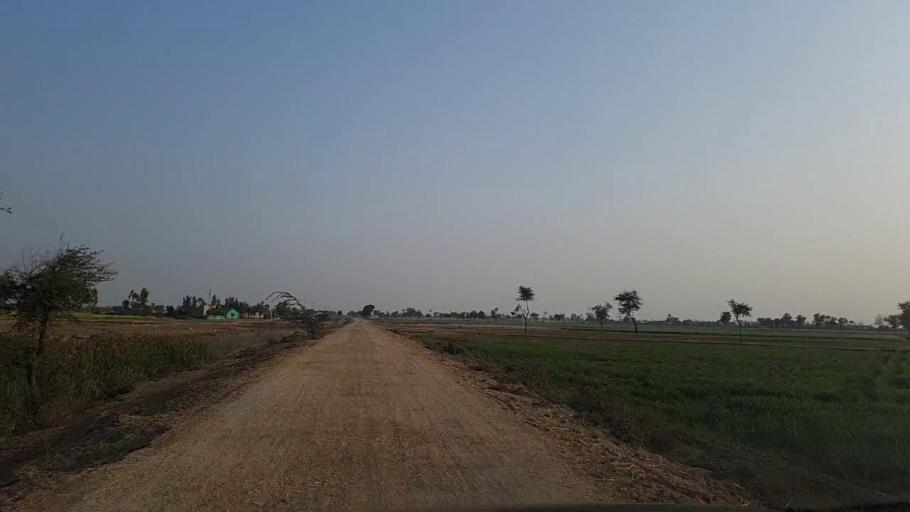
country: PK
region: Sindh
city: Daur
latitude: 26.4009
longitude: 68.3885
